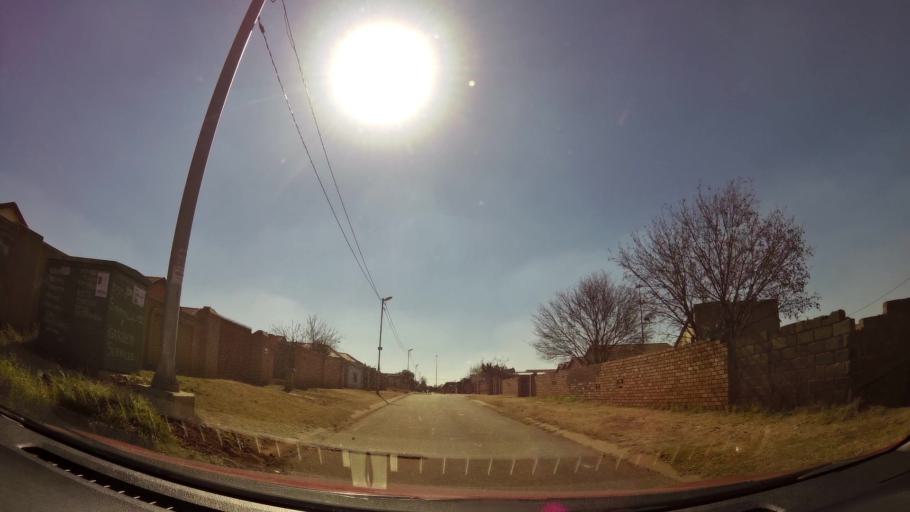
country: ZA
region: Gauteng
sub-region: City of Johannesburg Metropolitan Municipality
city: Soweto
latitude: -26.2474
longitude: 27.8059
